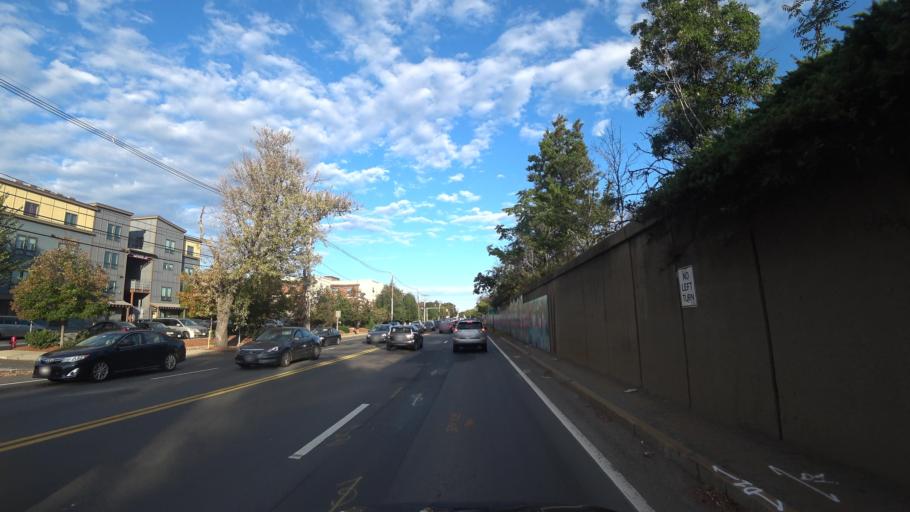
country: US
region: Massachusetts
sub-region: Middlesex County
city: Somerville
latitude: 42.3962
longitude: -71.0897
